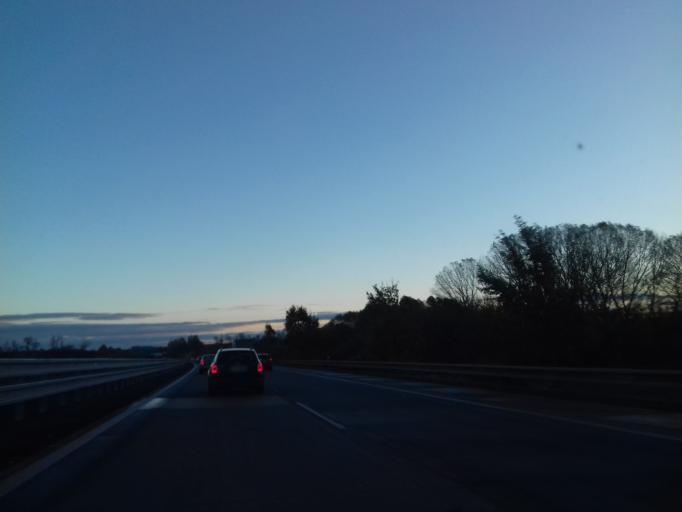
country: CZ
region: South Moravian
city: Rousinov
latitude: 49.2034
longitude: 16.9061
